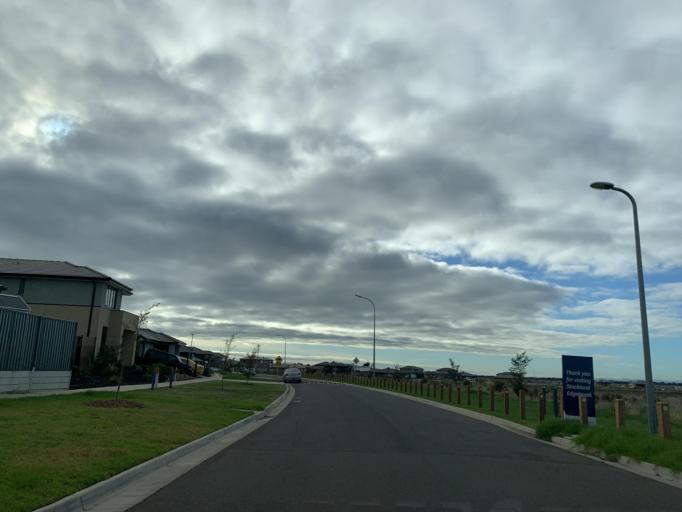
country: AU
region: Victoria
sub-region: Casey
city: Cranbourne East
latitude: -38.1273
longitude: 145.3541
